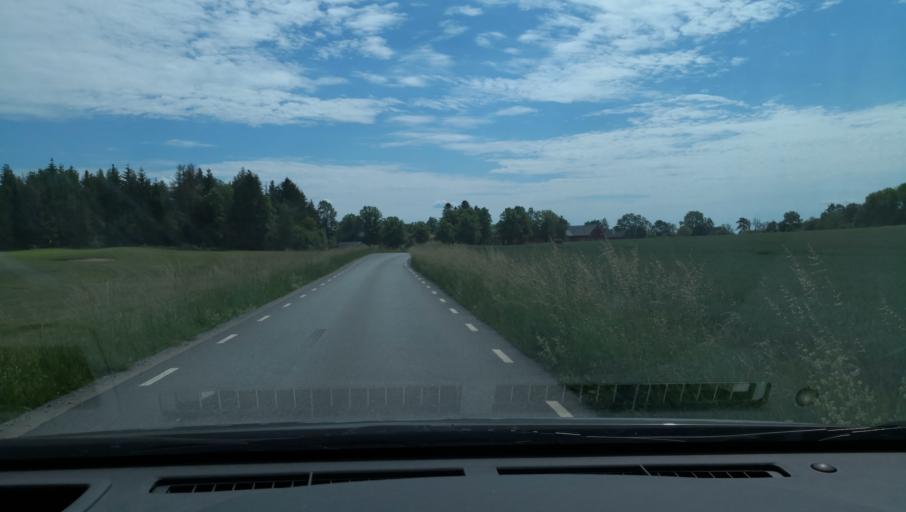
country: SE
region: Uppsala
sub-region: Habo Kommun
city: Balsta
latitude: 59.6993
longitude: 17.4785
